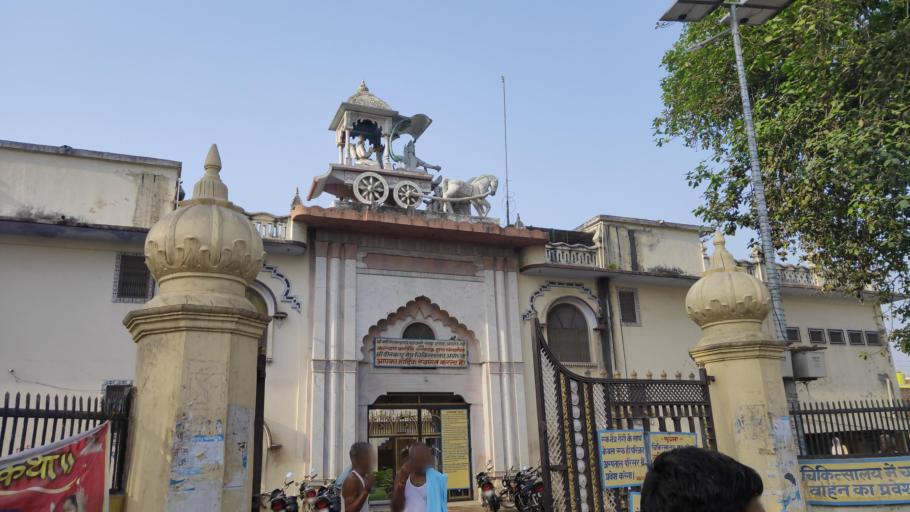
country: IN
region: Uttar Pradesh
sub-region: Faizabad
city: Ayodhya
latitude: 26.8011
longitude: 82.2125
